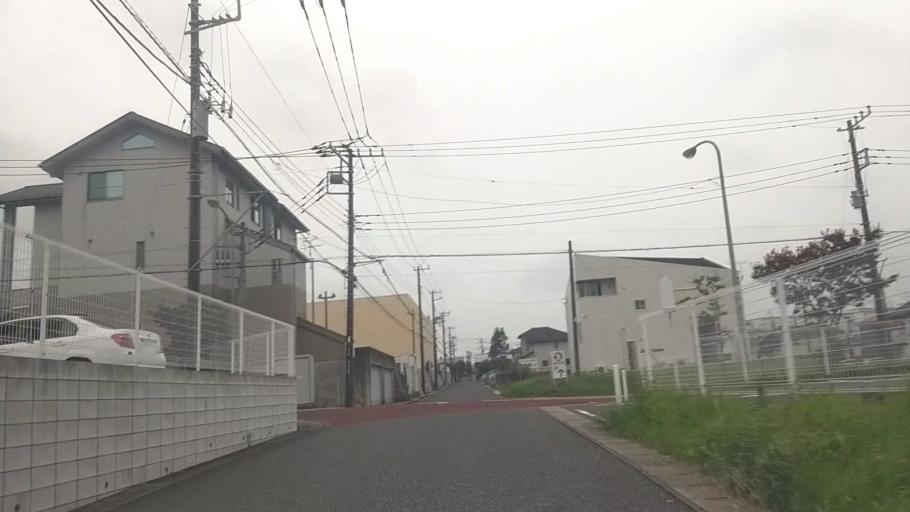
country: JP
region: Chiba
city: Kisarazu
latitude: 35.3814
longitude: 139.9656
